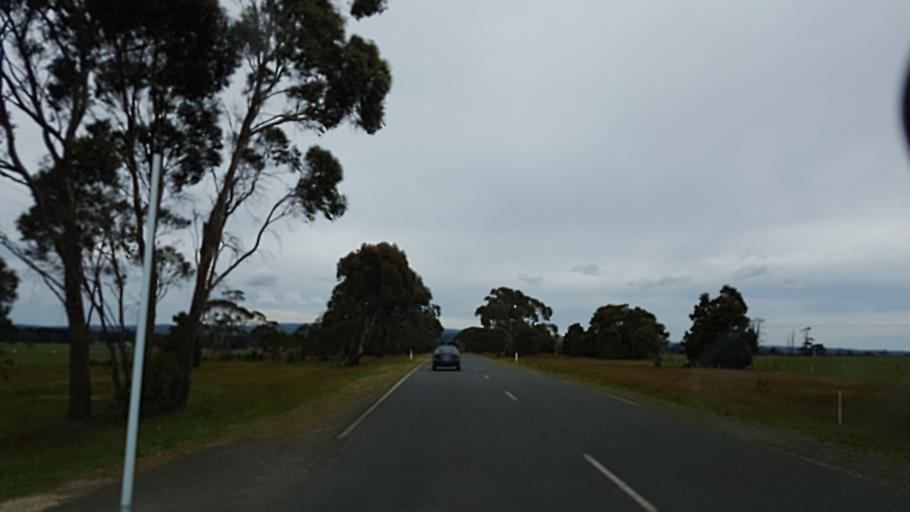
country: AU
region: Victoria
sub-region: Moorabool
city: Bacchus Marsh
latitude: -37.6203
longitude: 144.2113
